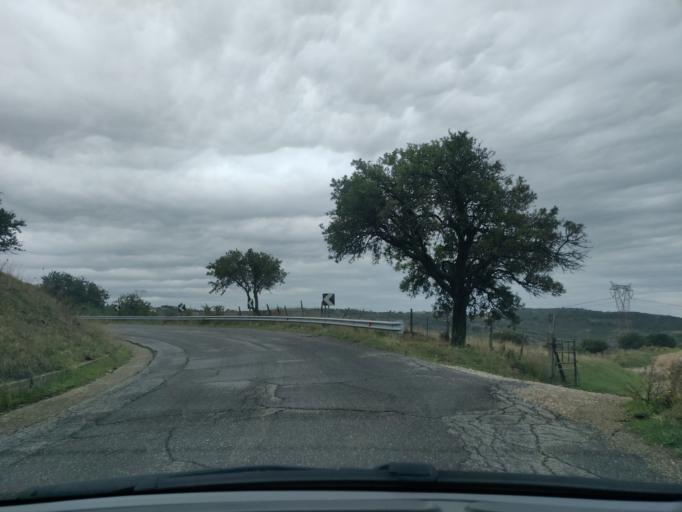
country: IT
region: Latium
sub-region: Citta metropolitana di Roma Capitale
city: Aurelia
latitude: 42.1298
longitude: 11.8477
